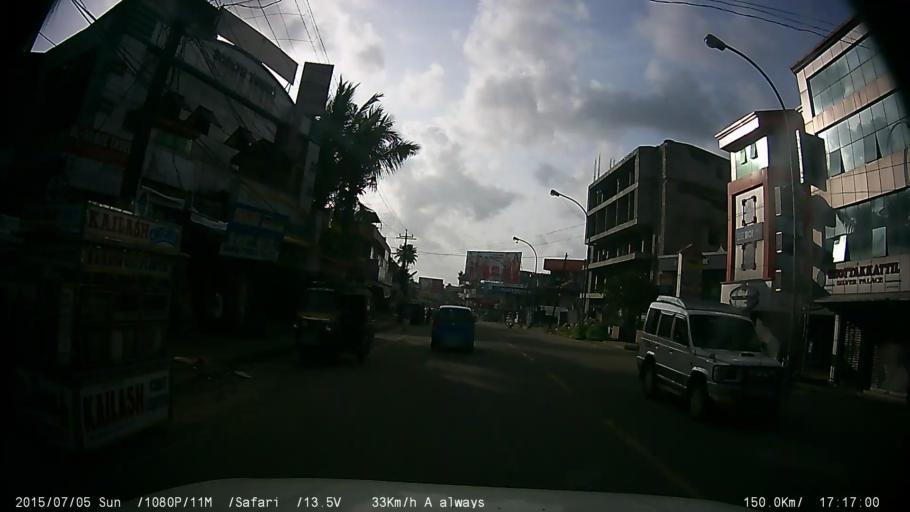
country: IN
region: Kerala
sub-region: Ernakulam
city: Perumpavur
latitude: 10.1161
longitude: 76.4768
